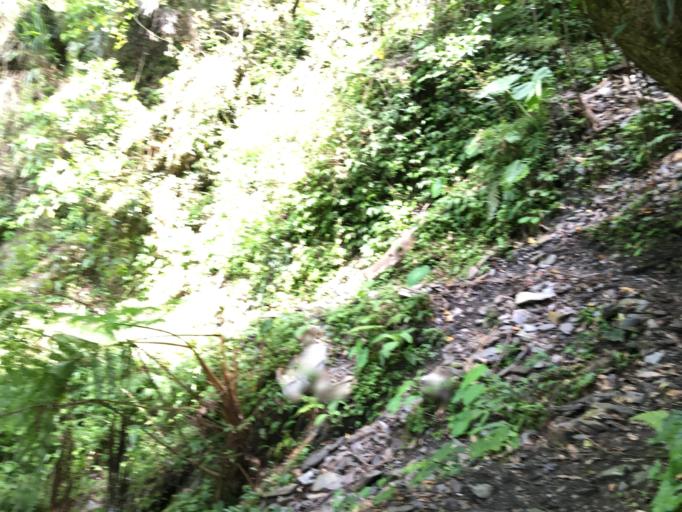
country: TW
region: Taiwan
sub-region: Yilan
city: Yilan
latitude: 24.4231
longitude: 121.7003
